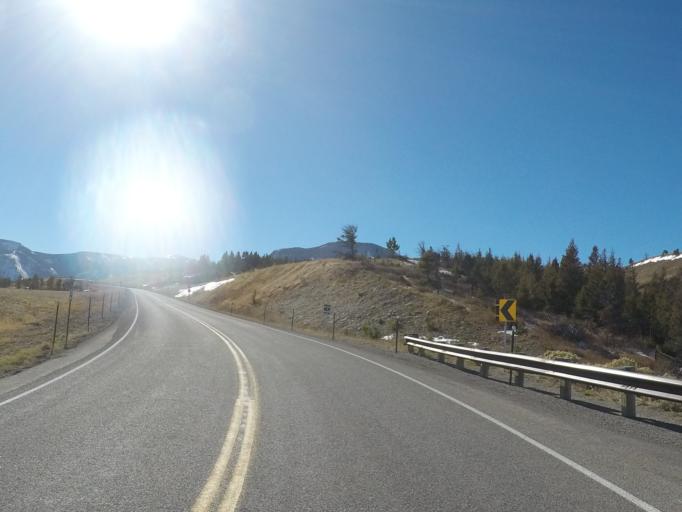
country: US
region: Wyoming
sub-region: Park County
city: Cody
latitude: 44.7295
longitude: -109.3112
